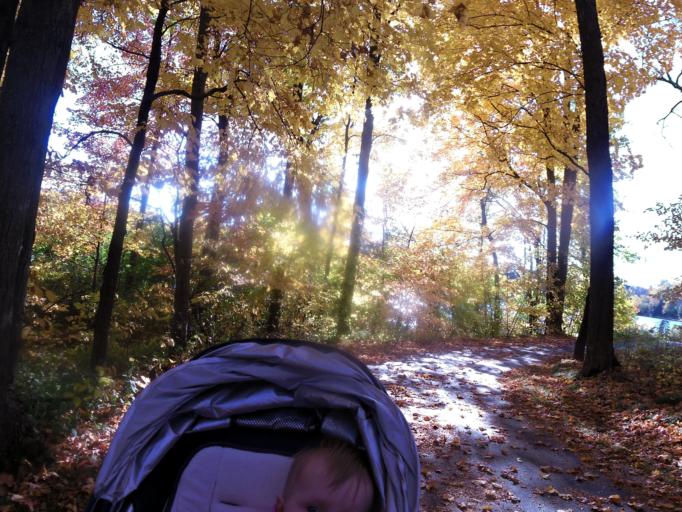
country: US
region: Minnesota
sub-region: Scott County
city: Prior Lake
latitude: 44.7018
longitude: -93.4381
